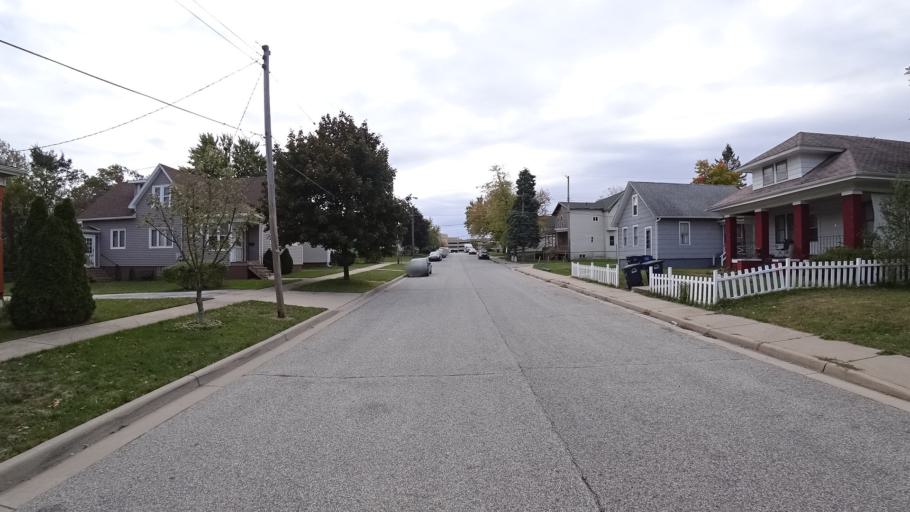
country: US
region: Indiana
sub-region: LaPorte County
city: Michigan City
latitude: 41.7092
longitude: -86.9026
